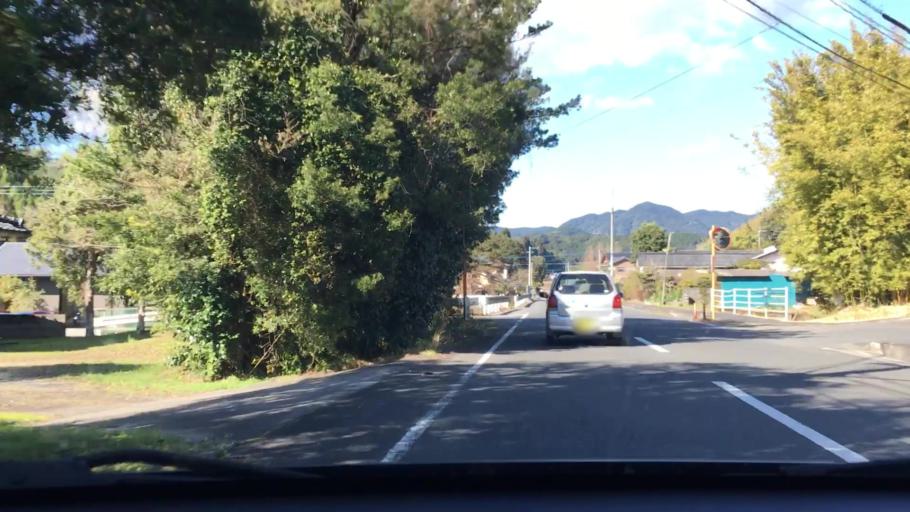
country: JP
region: Kagoshima
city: Ijuin
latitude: 31.6904
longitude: 130.4654
